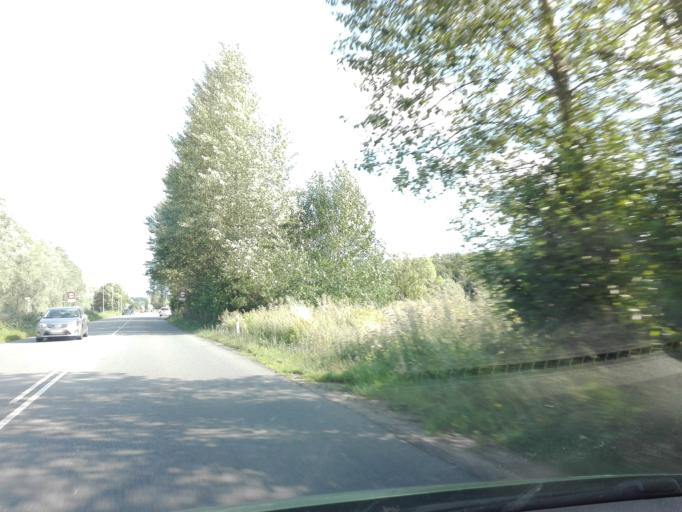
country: DK
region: Central Jutland
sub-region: Arhus Kommune
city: Lystrup
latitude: 56.2138
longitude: 10.2345
